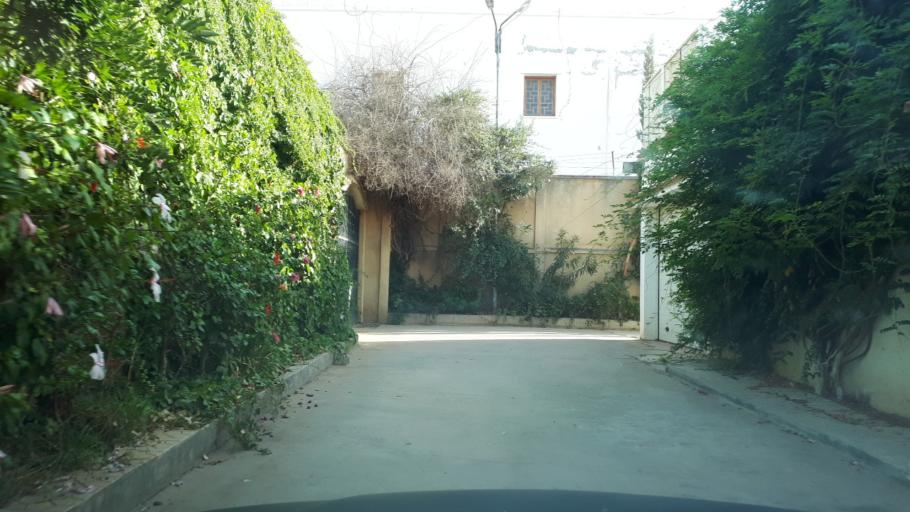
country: DZ
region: Tipaza
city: Zeralda
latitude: 36.7249
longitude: 2.8919
